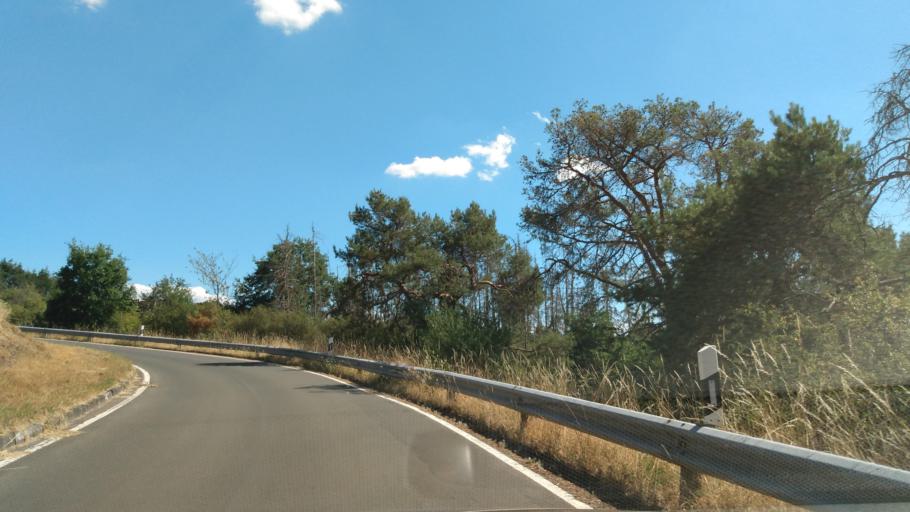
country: DE
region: Rheinland-Pfalz
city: Landscheid
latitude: 49.9976
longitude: 6.7752
